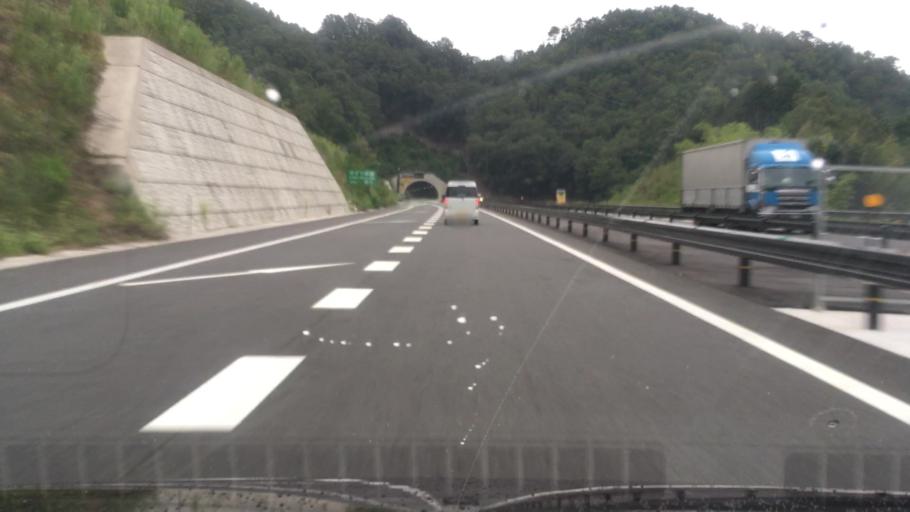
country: JP
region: Hyogo
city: Toyooka
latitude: 35.4323
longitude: 134.7676
